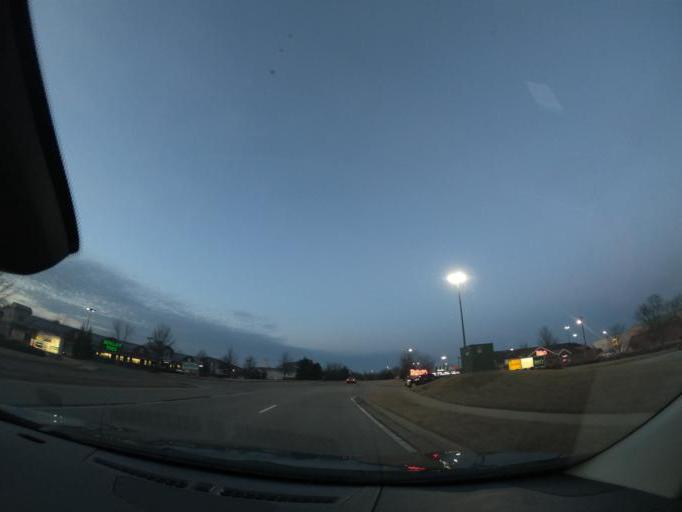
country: US
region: Kentucky
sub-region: Jefferson County
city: Worthington
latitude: 38.2988
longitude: -85.5602
